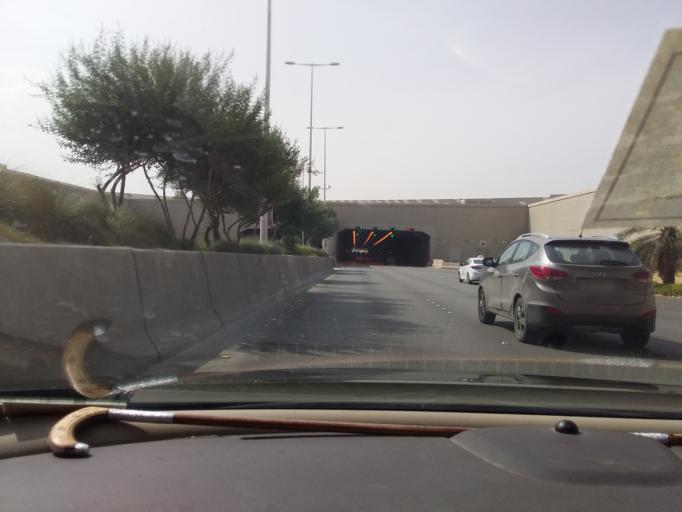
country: SA
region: Ar Riyad
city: Riyadh
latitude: 24.7328
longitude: 46.7324
